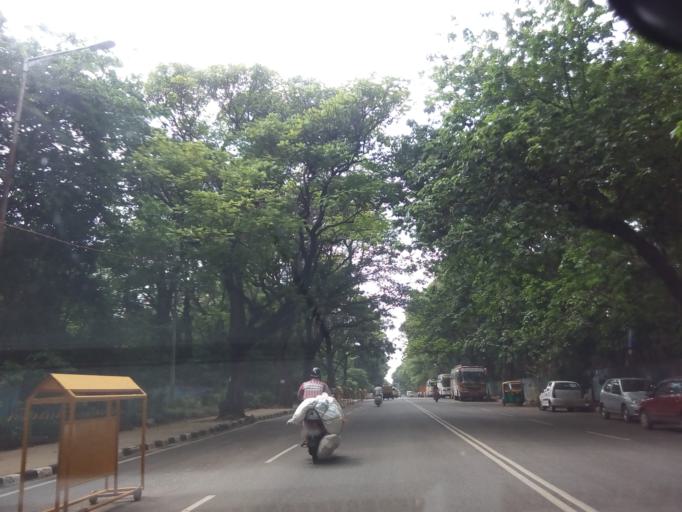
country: IN
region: Karnataka
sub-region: Bangalore Urban
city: Bangalore
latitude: 13.0155
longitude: 77.5594
